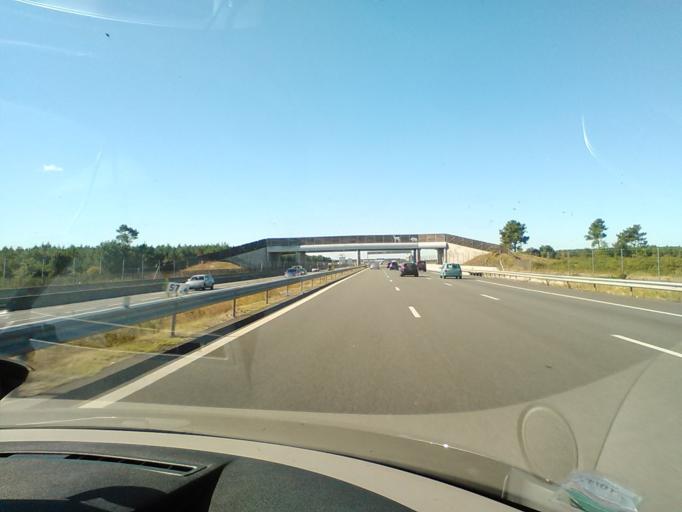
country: FR
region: Aquitaine
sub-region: Departement des Landes
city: Pissos
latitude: 44.3566
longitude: -0.8542
